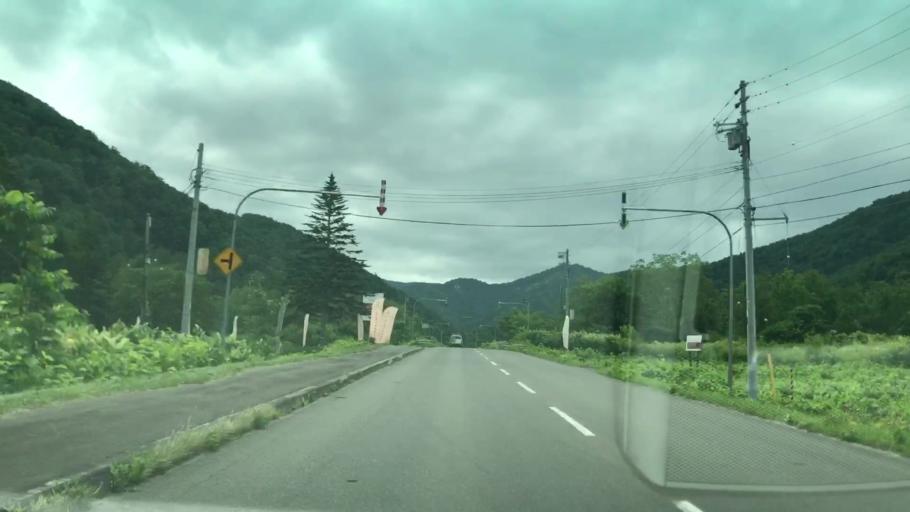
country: JP
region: Hokkaido
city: Yoichi
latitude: 43.0285
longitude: 140.8660
